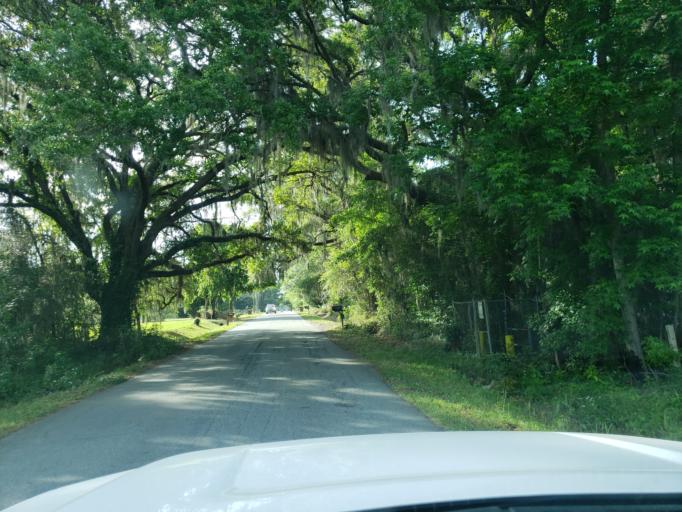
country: US
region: Georgia
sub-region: Chatham County
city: Georgetown
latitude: 32.0111
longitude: -81.2334
